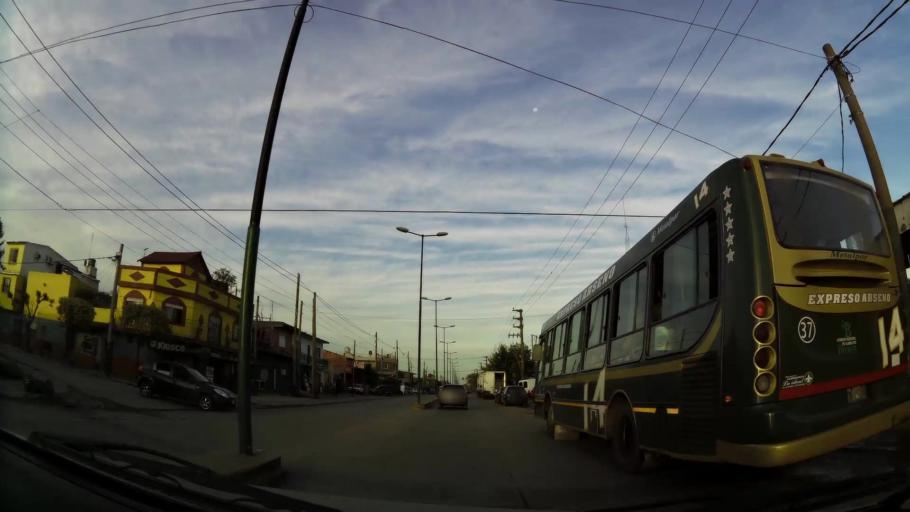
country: AR
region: Buenos Aires
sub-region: Partido de Almirante Brown
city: Adrogue
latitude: -34.7785
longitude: -58.3334
